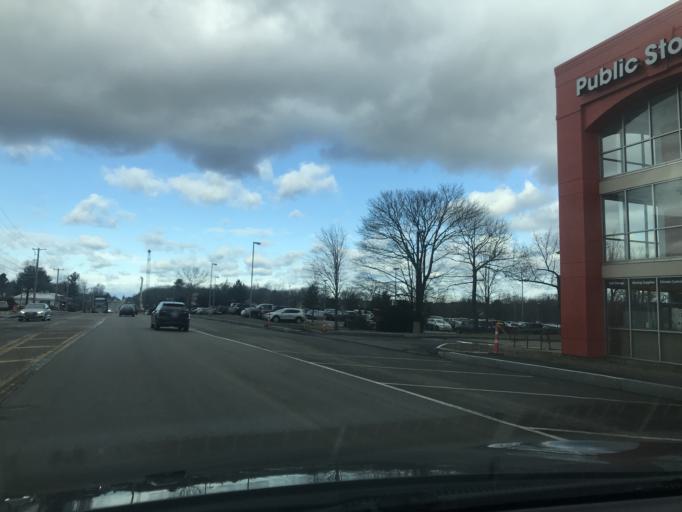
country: US
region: Massachusetts
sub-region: Plymouth County
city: Rockland
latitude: 42.1538
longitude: -70.9551
